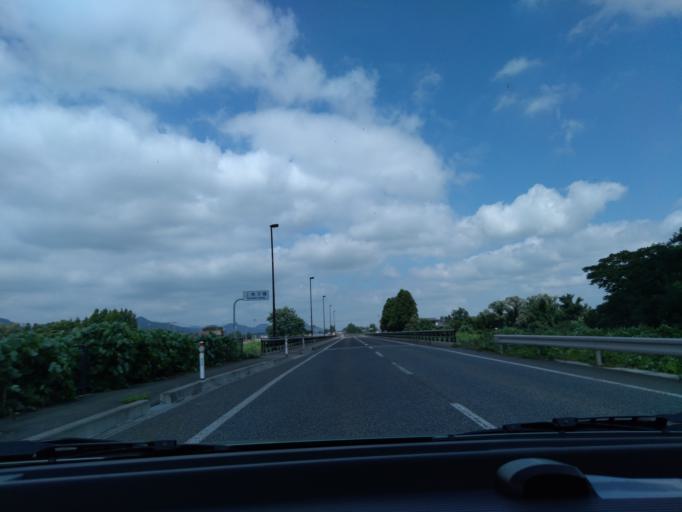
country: JP
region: Iwate
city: Hanamaki
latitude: 39.3776
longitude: 141.0559
